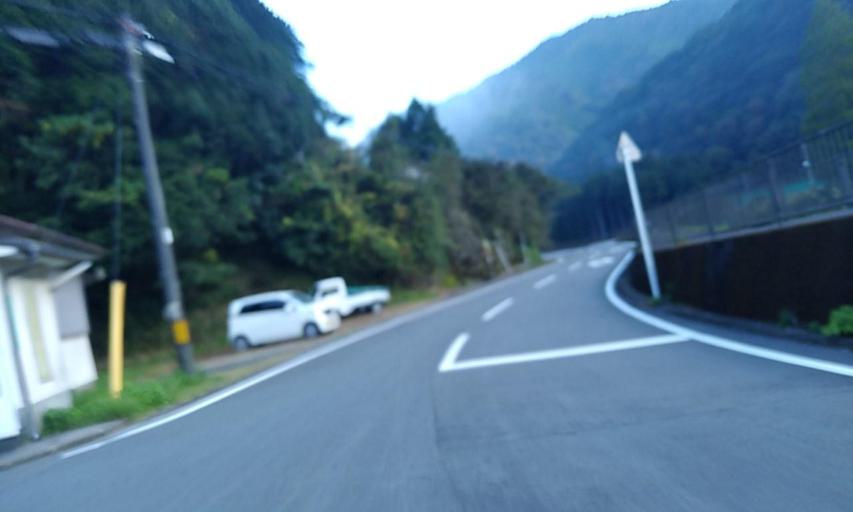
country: JP
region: Wakayama
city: Shingu
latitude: 33.7300
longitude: 135.9099
